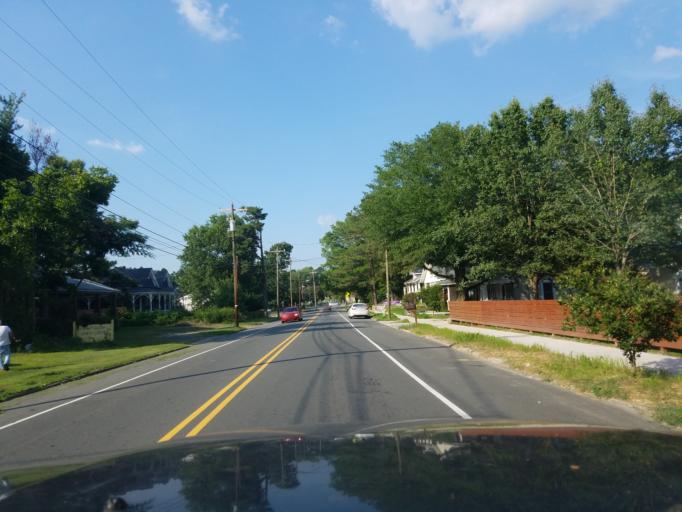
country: US
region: North Carolina
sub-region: Durham County
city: Durham
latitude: 35.9909
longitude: -78.9235
